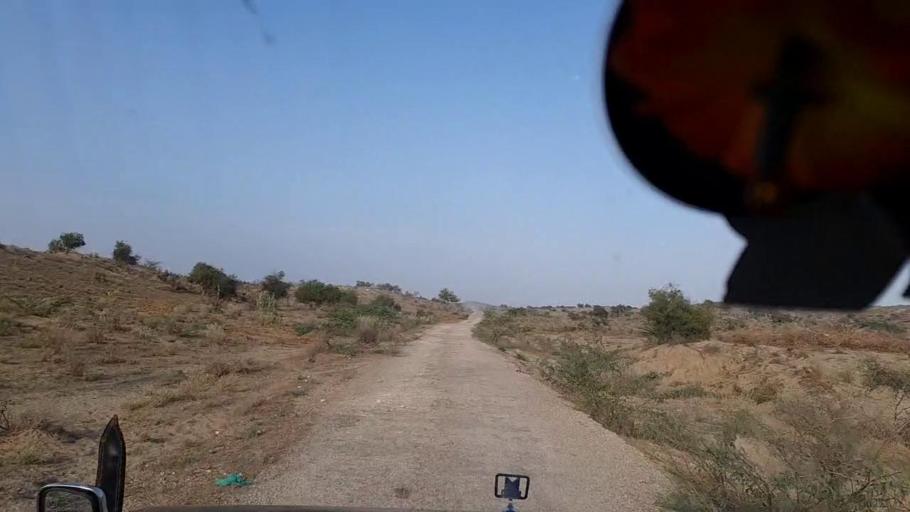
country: PK
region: Sindh
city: Diplo
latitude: 24.5612
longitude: 69.4808
